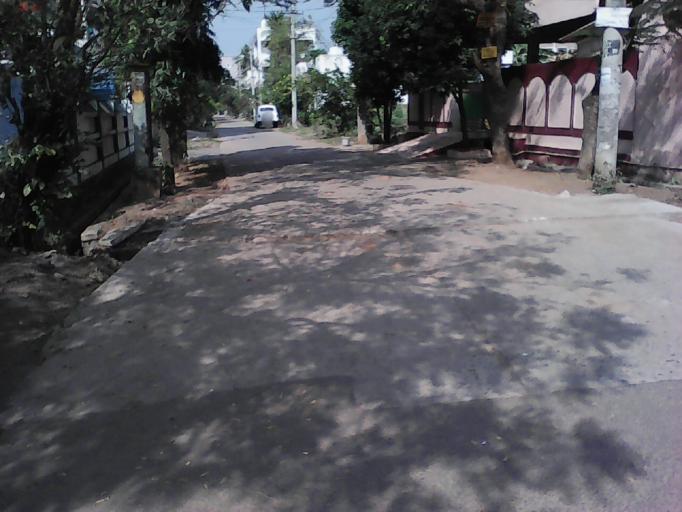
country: IN
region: Andhra Pradesh
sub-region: Guntur
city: Bhattiprolu
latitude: 16.2381
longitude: 80.6576
